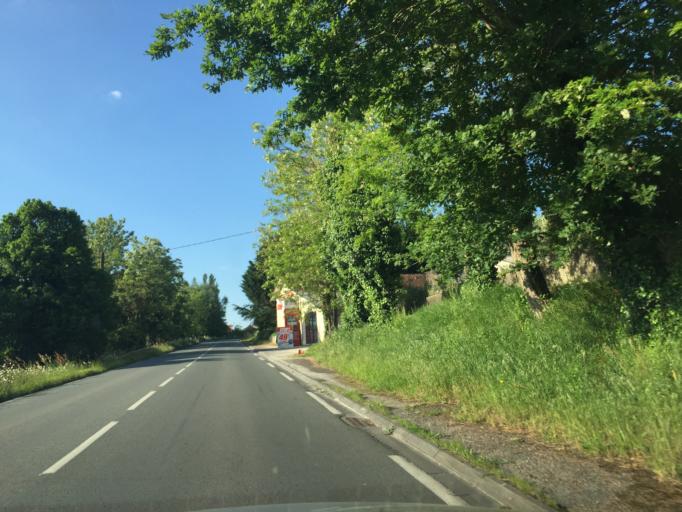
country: FR
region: Aquitaine
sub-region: Departement de la Dordogne
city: La Roche-Chalais
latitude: 45.1618
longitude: 0.0078
